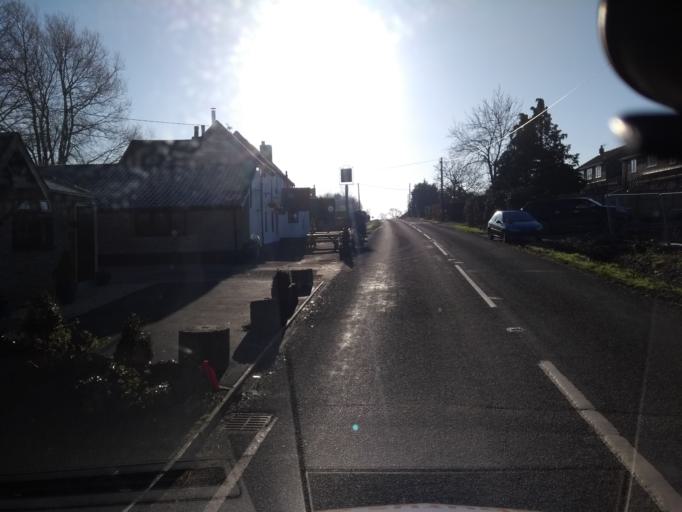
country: GB
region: England
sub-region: Somerset
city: Wincanton
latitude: 51.0839
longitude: -2.3913
